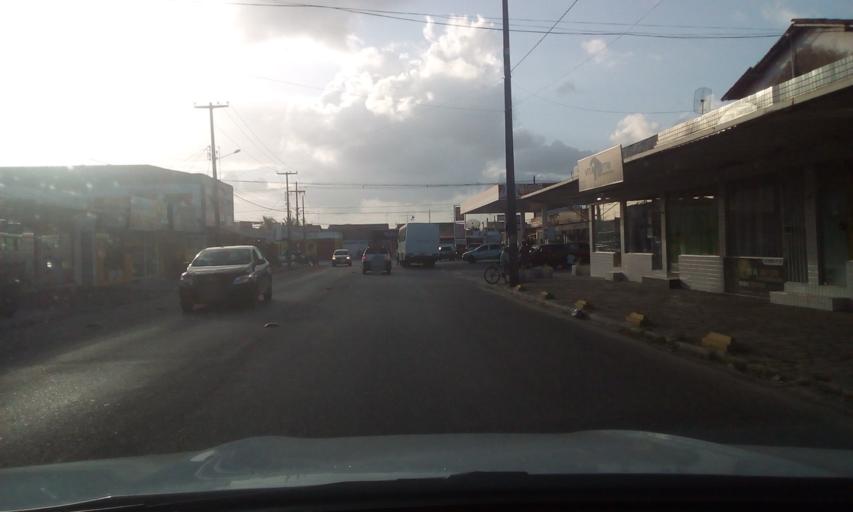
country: BR
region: Paraiba
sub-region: Conde
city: Conde
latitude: -7.2064
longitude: -34.8459
